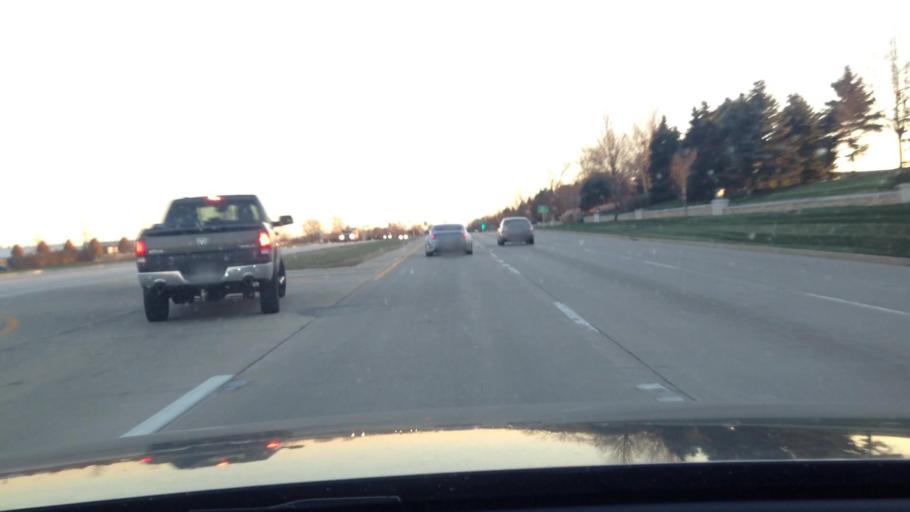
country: US
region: Illinois
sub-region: McHenry County
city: Huntley
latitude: 42.1450
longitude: -88.4329
